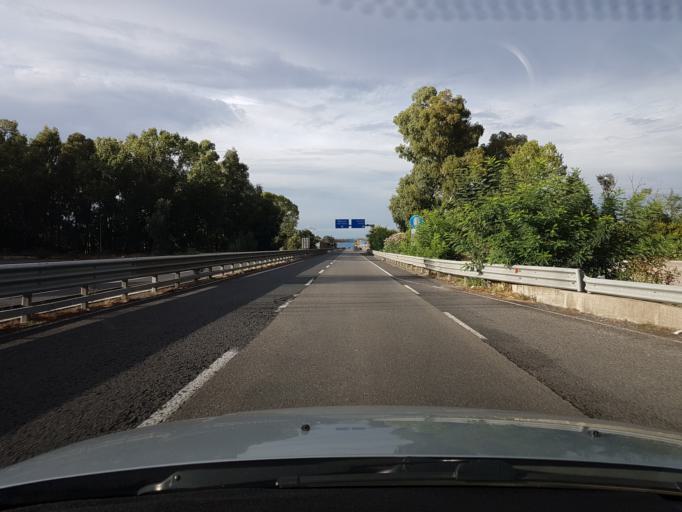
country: IT
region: Sardinia
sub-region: Provincia di Oristano
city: Abbasanta
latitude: 40.1103
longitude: 8.7932
